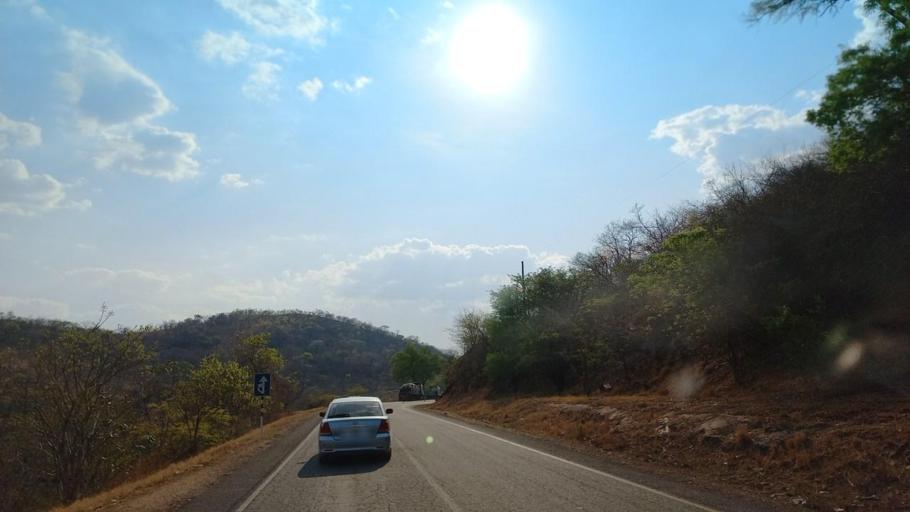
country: ZM
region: Lusaka
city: Luangwa
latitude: -14.9851
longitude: 30.1975
